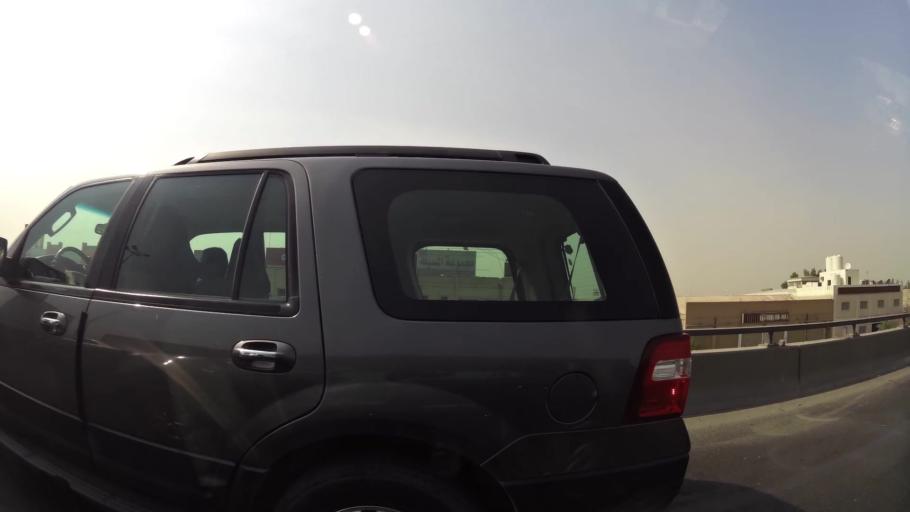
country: KW
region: Al Asimah
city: Ar Rabiyah
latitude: 29.3208
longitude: 47.9383
